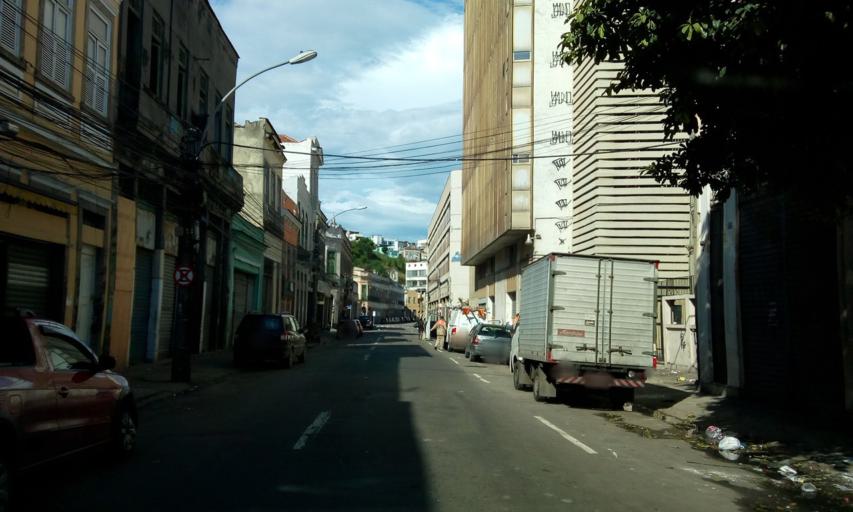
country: BR
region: Rio de Janeiro
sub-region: Rio De Janeiro
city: Rio de Janeiro
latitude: -22.9008
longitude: -43.1886
